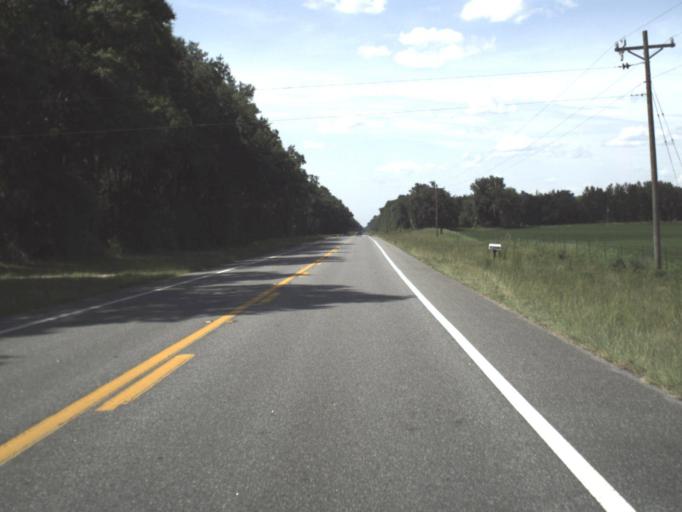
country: US
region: Florida
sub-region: Alachua County
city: High Springs
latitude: 29.8169
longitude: -82.7414
